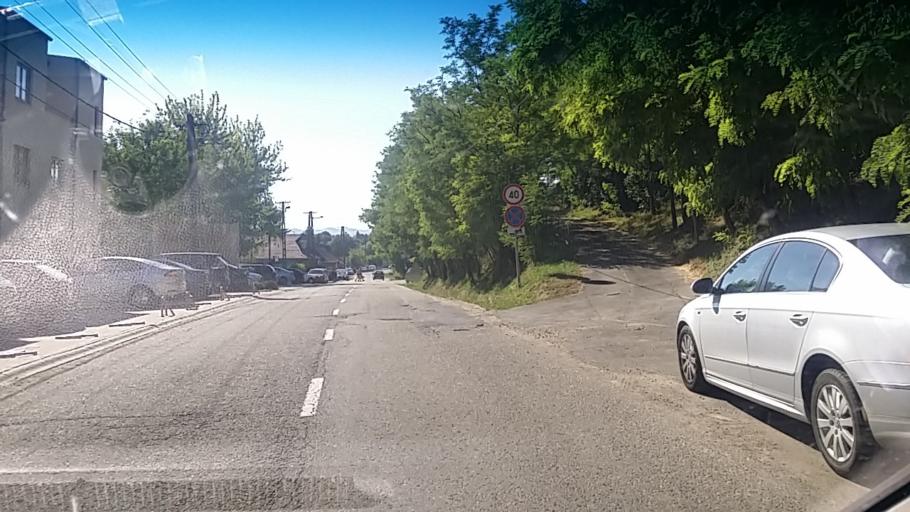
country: HU
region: Nograd
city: Retsag
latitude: 47.9231
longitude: 19.1795
